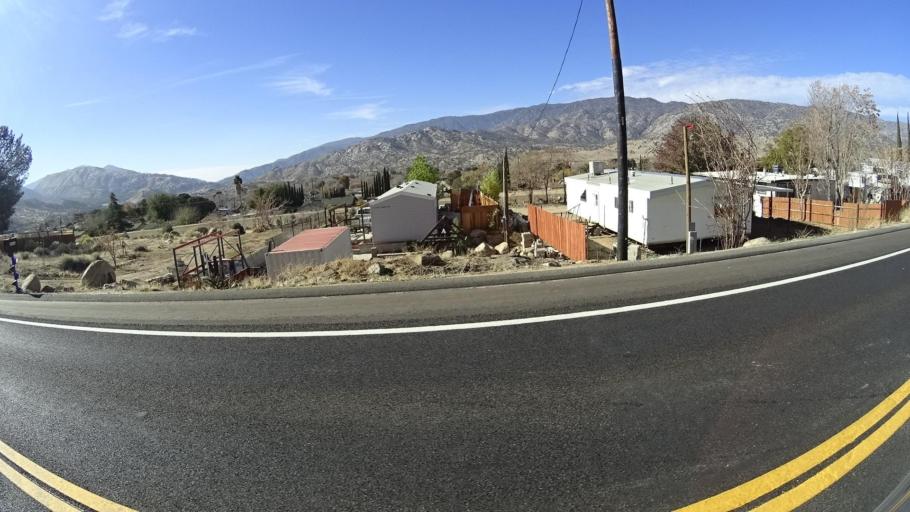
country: US
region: California
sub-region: Kern County
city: Lake Isabella
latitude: 35.6144
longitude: -118.4670
